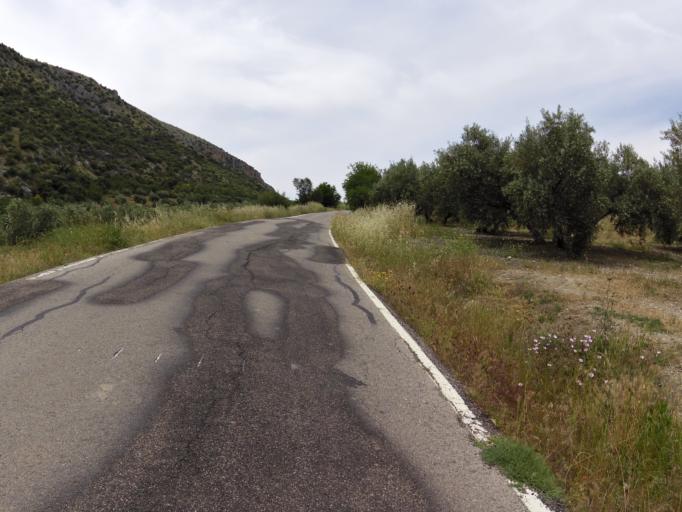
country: ES
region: Andalusia
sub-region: Province of Cordoba
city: Luque
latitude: 37.5197
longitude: -4.2267
